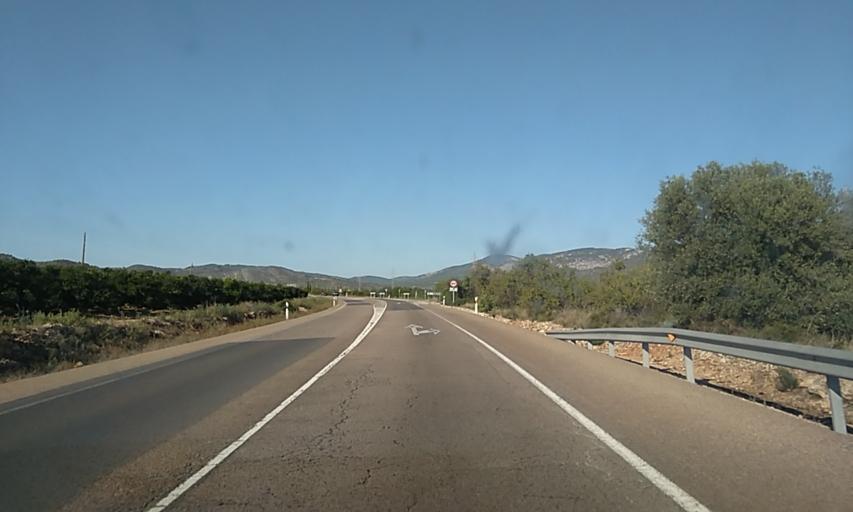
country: ES
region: Valencia
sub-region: Provincia de Castello
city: Torreblanca
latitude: 40.2442
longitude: 0.2313
